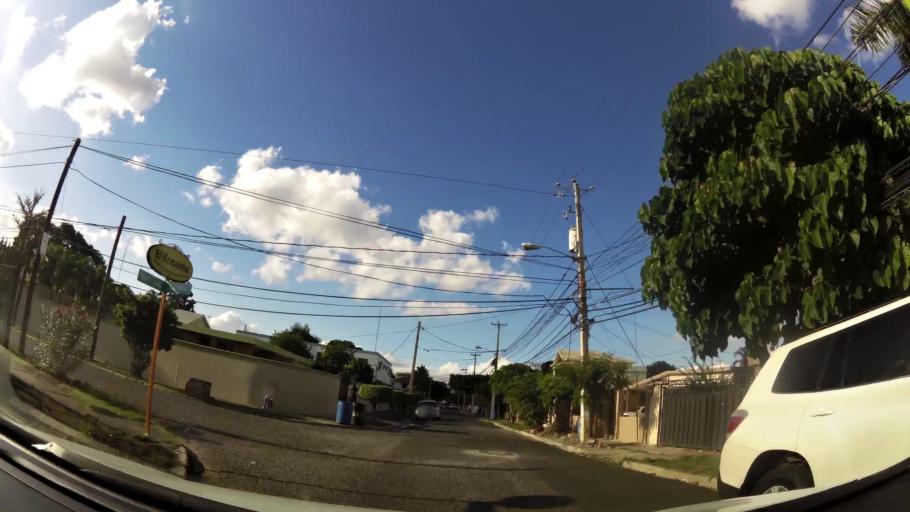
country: DO
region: Santiago
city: Santiago de los Caballeros
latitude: 19.4603
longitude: -70.6953
